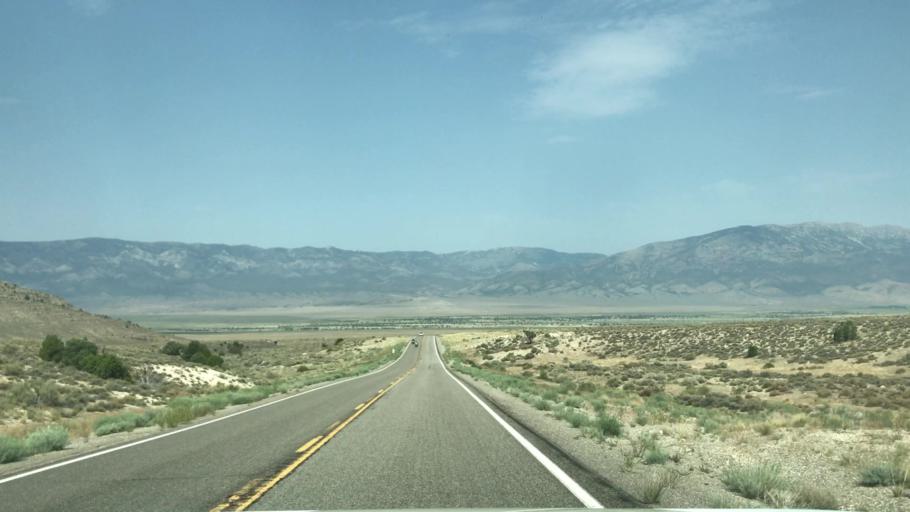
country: US
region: Nevada
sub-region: White Pine County
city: McGill
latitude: 39.1744
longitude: -114.3782
